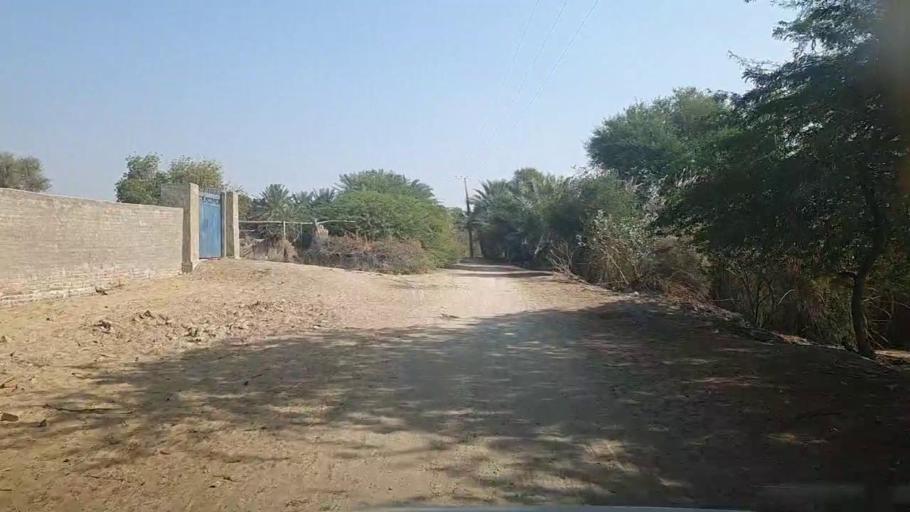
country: PK
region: Sindh
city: Kandiari
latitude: 26.9408
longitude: 68.5399
